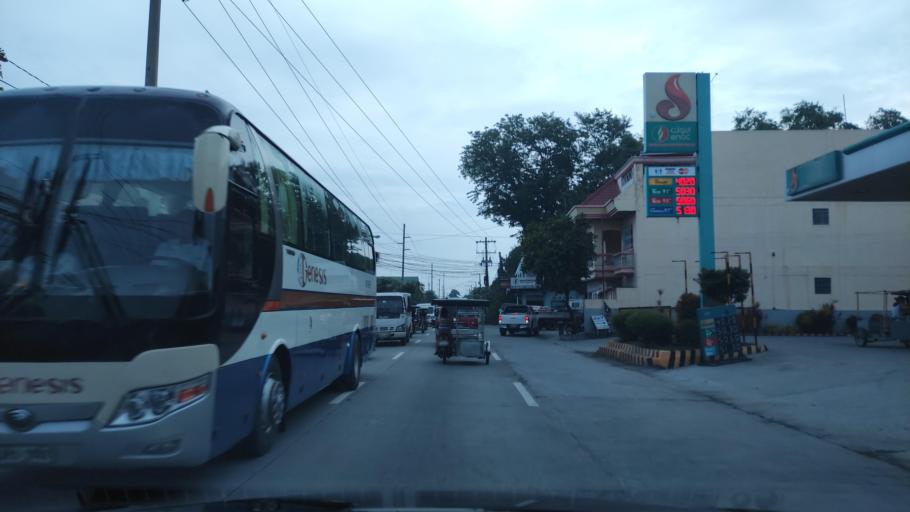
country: PH
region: Central Luzon
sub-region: Province of Pampanga
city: Santa Ana
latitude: 15.0976
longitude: 120.7679
